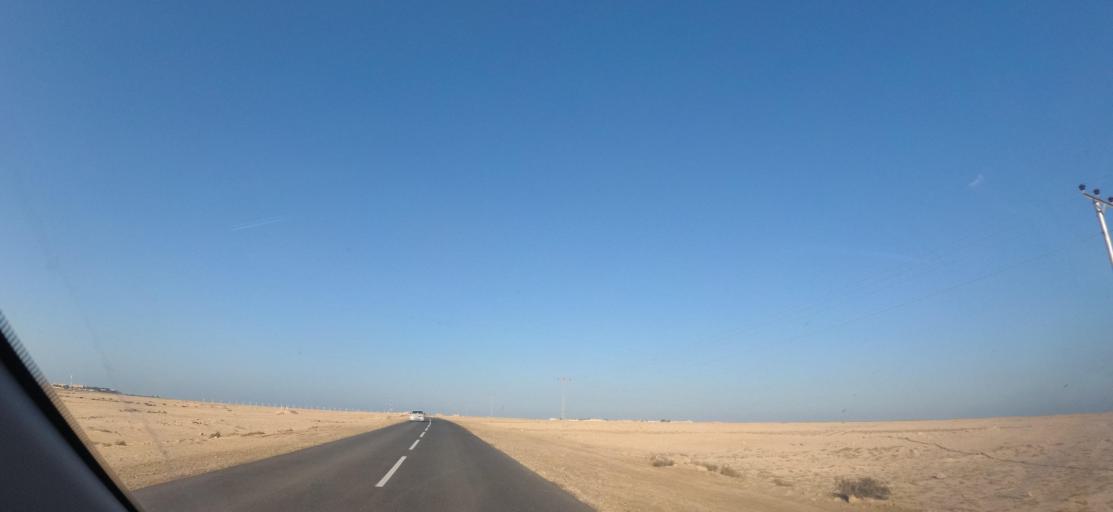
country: QA
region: Madinat ash Shamal
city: Ar Ru'ays
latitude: 26.1428
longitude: 51.2453
